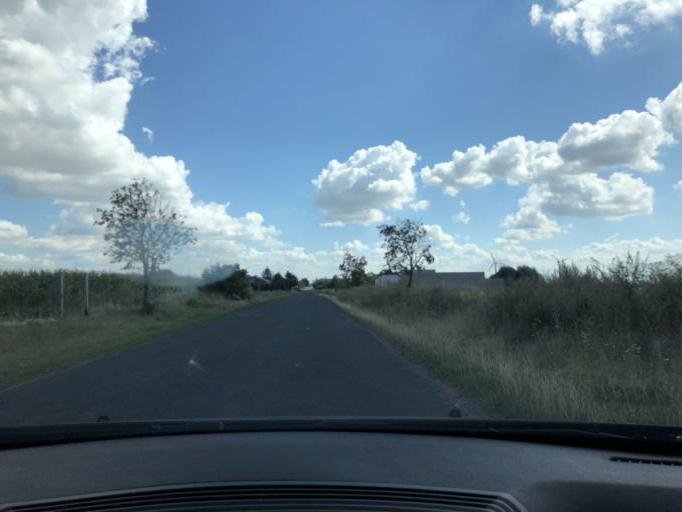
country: PL
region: Lodz Voivodeship
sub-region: Powiat wieruszowski
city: Walichnowy
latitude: 51.2612
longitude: 18.3769
